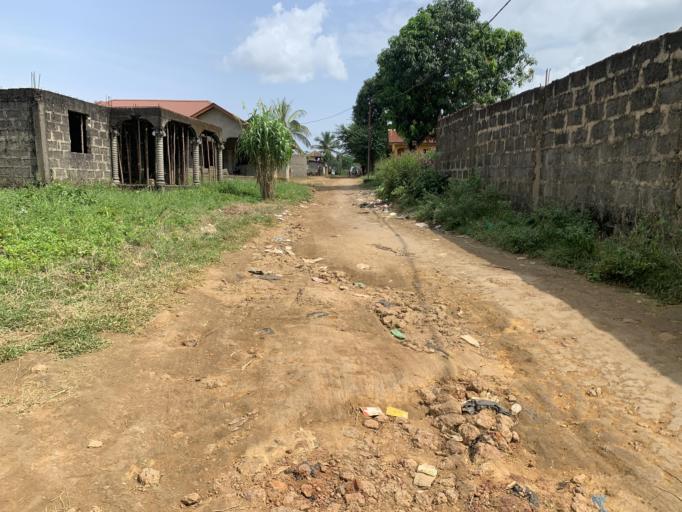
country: SL
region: Western Area
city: Hastings
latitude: 8.3902
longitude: -13.1391
